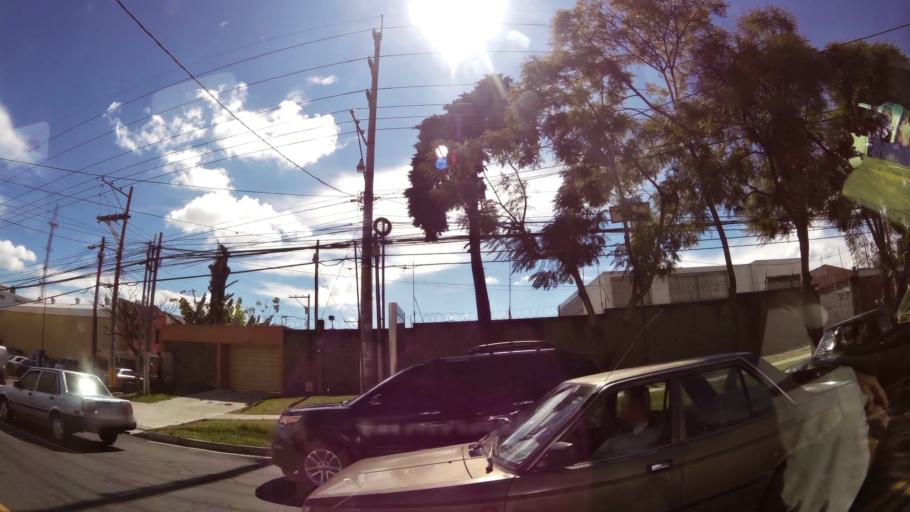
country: GT
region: Guatemala
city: Mixco
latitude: 14.6316
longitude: -90.5607
